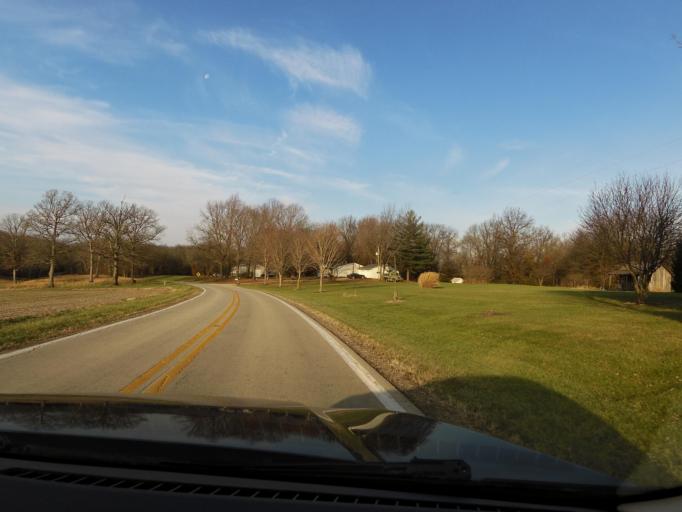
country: US
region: Illinois
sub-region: Fayette County
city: Vandalia
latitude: 38.9222
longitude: -89.2271
